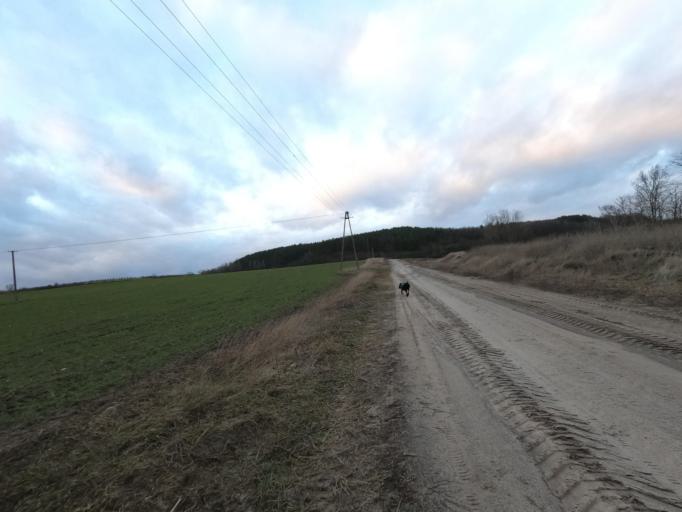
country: PL
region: Greater Poland Voivodeship
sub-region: Powiat pilski
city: Wyrzysk
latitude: 53.1141
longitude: 17.2035
